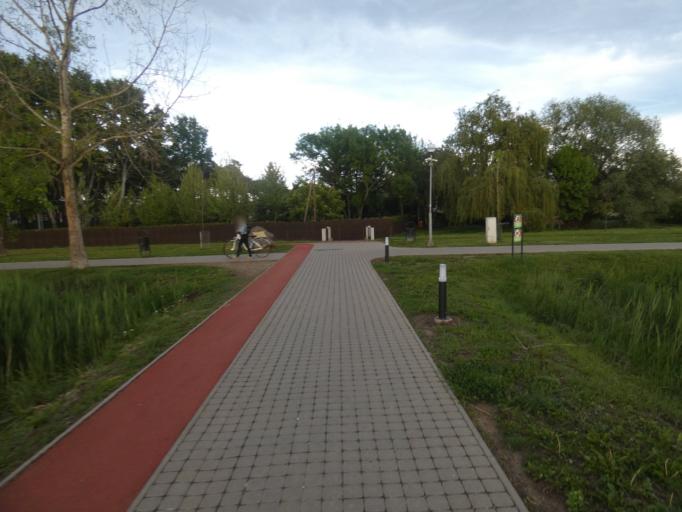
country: HU
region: Szabolcs-Szatmar-Bereg
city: Kotaj
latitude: 48.0038
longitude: 21.7293
